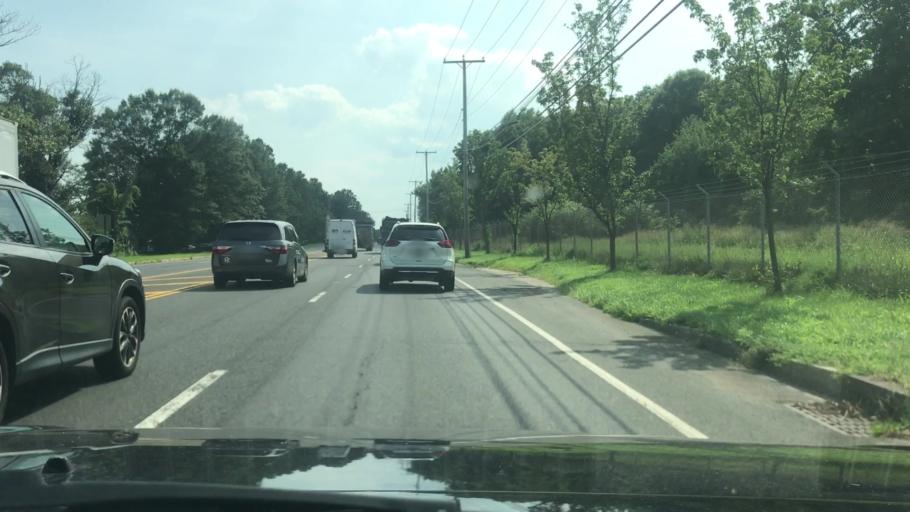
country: US
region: New Jersey
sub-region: Monmouth County
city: Tinton Falls
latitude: 40.2693
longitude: -74.0831
